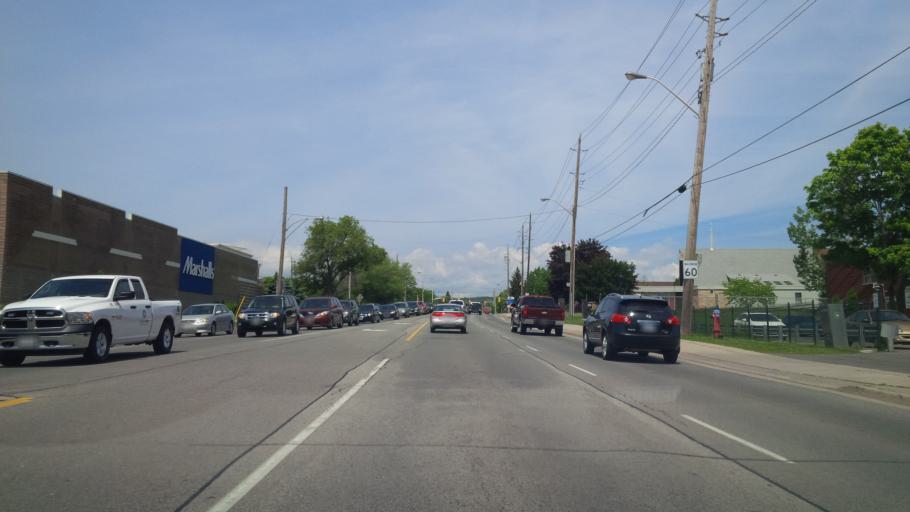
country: CA
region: Ontario
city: Burlington
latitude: 43.3446
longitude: -79.8261
